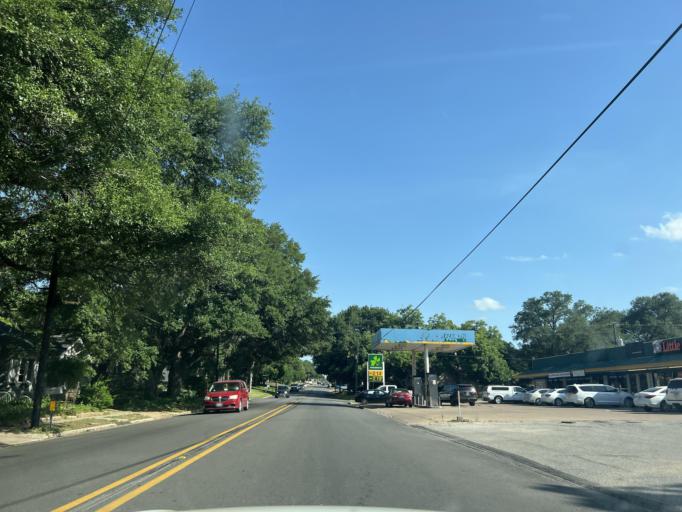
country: US
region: Texas
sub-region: Washington County
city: Brenham
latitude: 30.1541
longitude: -96.3979
